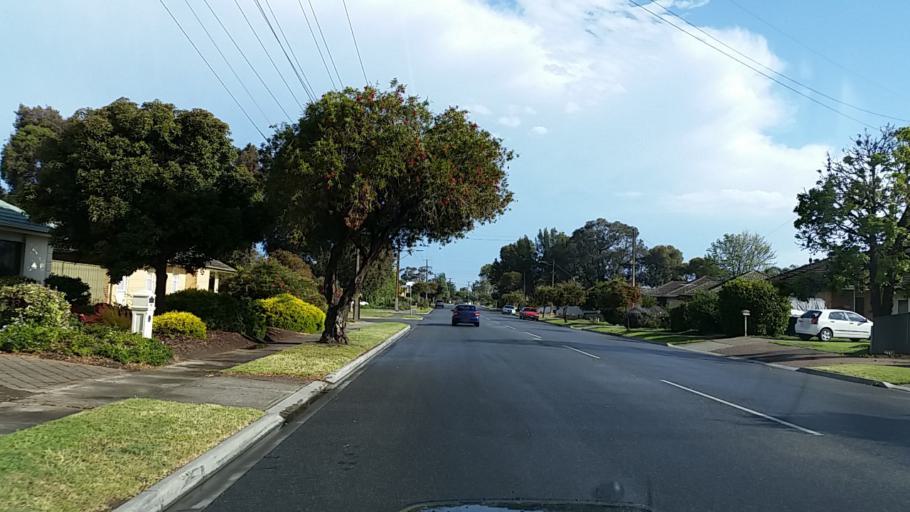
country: AU
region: South Australia
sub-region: Charles Sturt
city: Henley Beach
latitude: -34.9166
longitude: 138.5007
